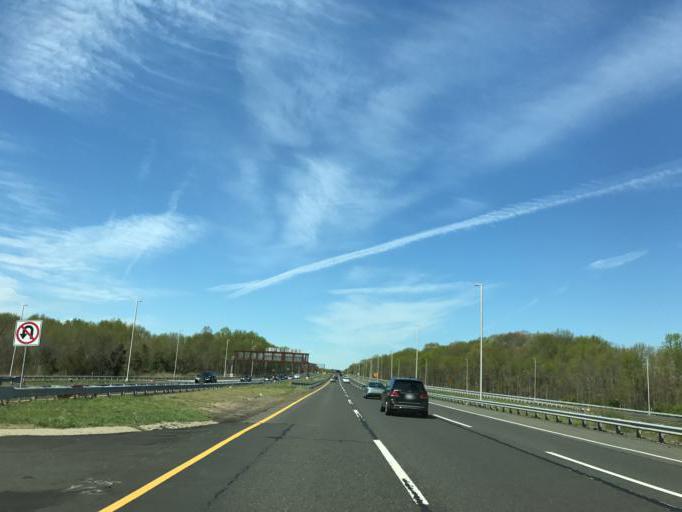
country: US
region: New Jersey
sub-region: Burlington County
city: Bordentown
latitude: 40.0972
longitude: -74.7347
